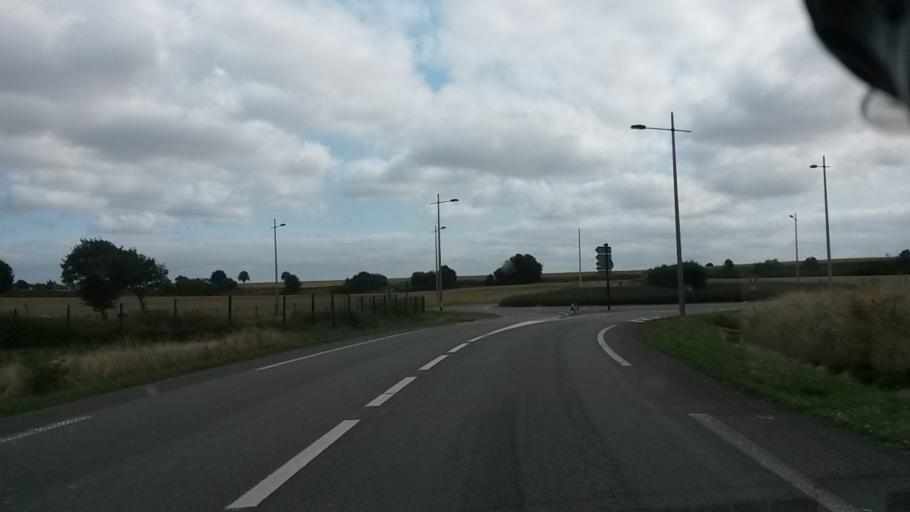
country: FR
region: Nord-Pas-de-Calais
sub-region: Departement du Pas-de-Calais
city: Bapaume
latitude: 50.1005
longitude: 2.8323
